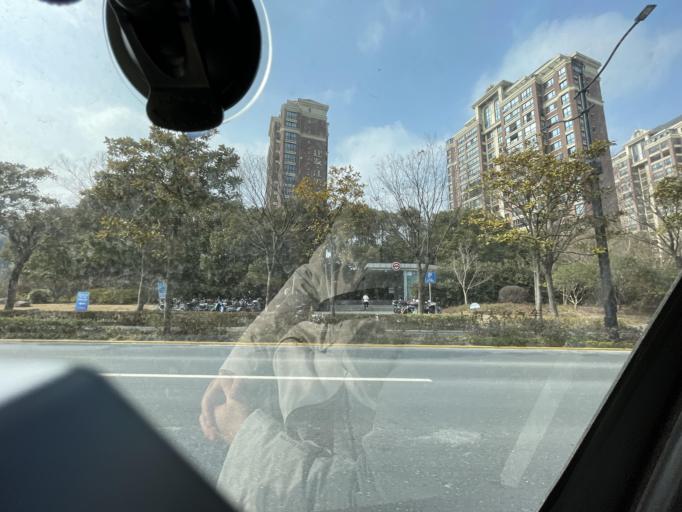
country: CN
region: Shanghai Shi
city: Yangpu
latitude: 31.3234
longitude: 121.5022
